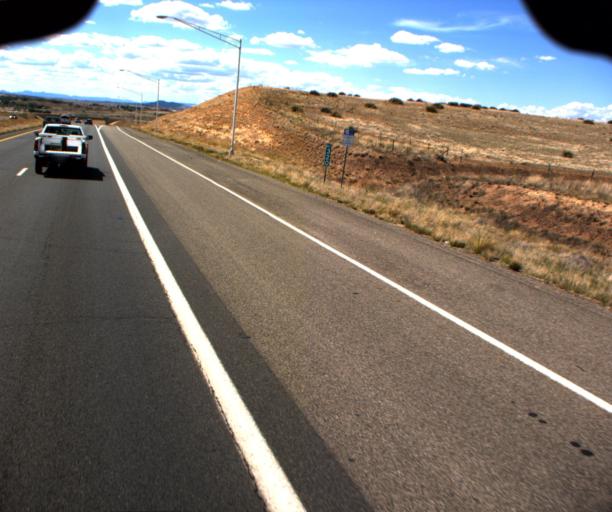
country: US
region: Arizona
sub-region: Yavapai County
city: Prescott Valley
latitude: 34.6330
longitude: -112.3914
